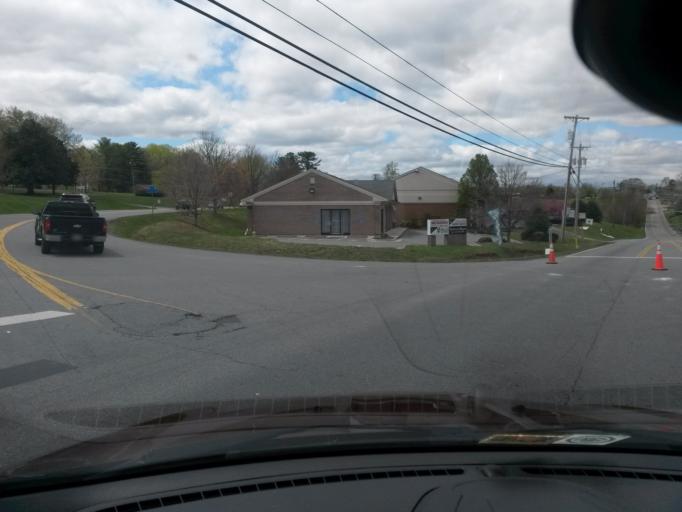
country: US
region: Virginia
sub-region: City of Lynchburg
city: West Lynchburg
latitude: 37.3993
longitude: -79.2082
